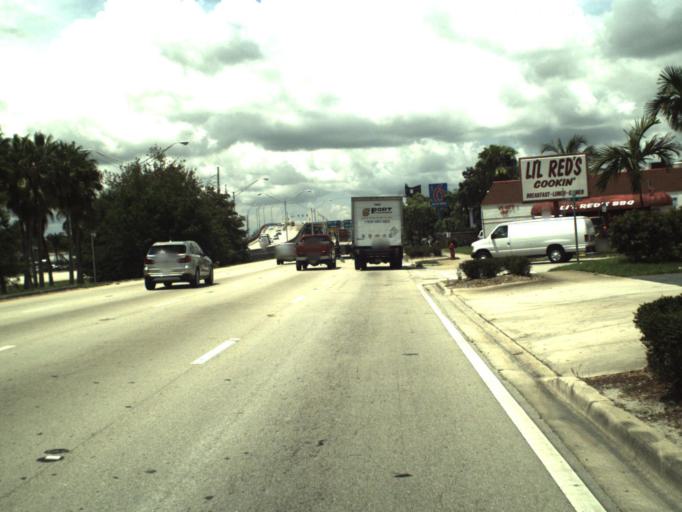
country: US
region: Florida
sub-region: Broward County
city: Fort Lauderdale
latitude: 26.0904
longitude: -80.1625
